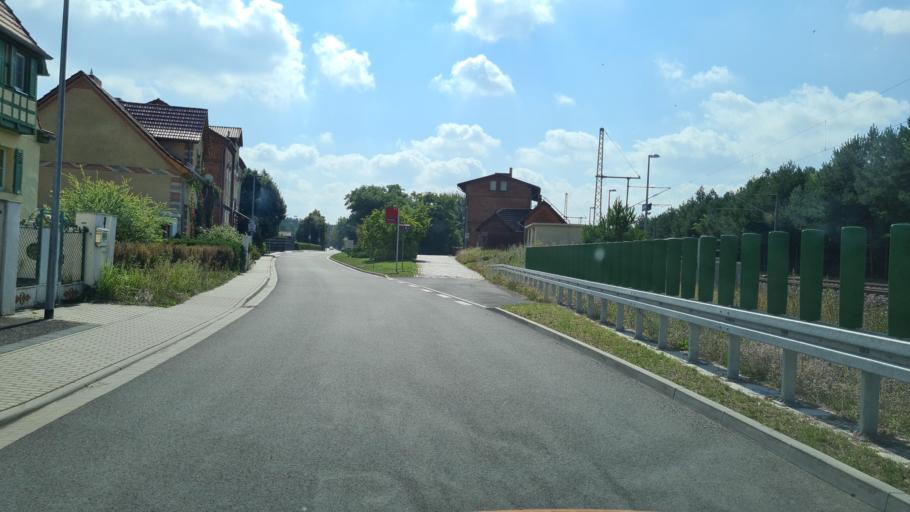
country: DE
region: Brandenburg
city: Sonnewalde
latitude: 51.7737
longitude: 13.6177
